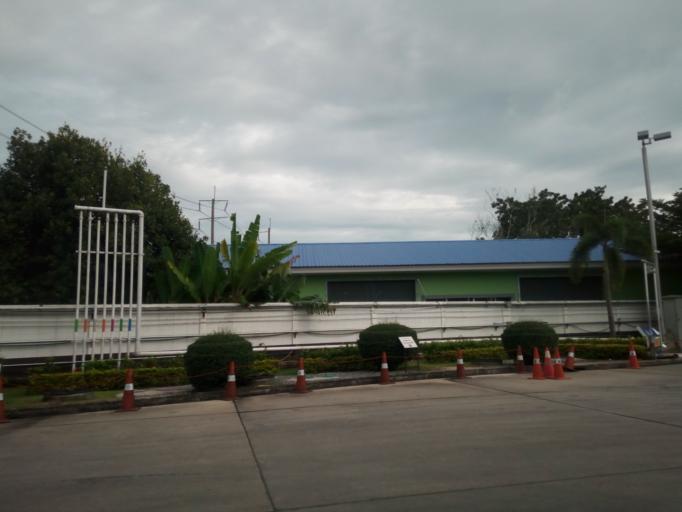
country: TH
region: Phuket
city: Thalang
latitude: 8.0045
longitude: 98.3446
